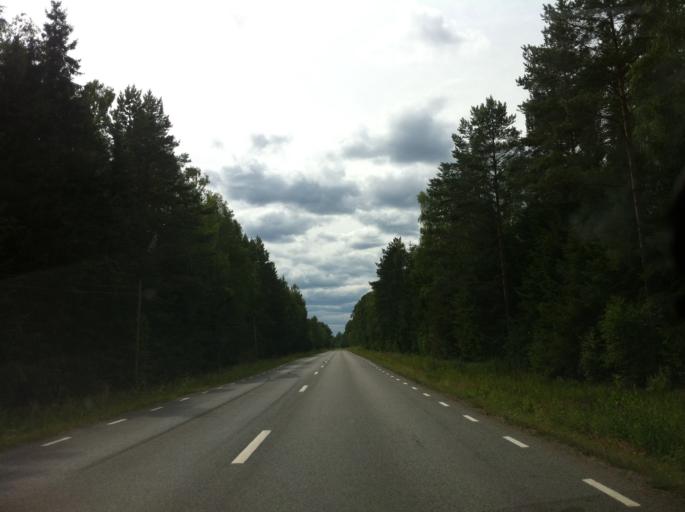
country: SE
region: Blekinge
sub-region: Olofstroms Kommun
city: Olofstroem
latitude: 56.4660
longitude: 14.6545
